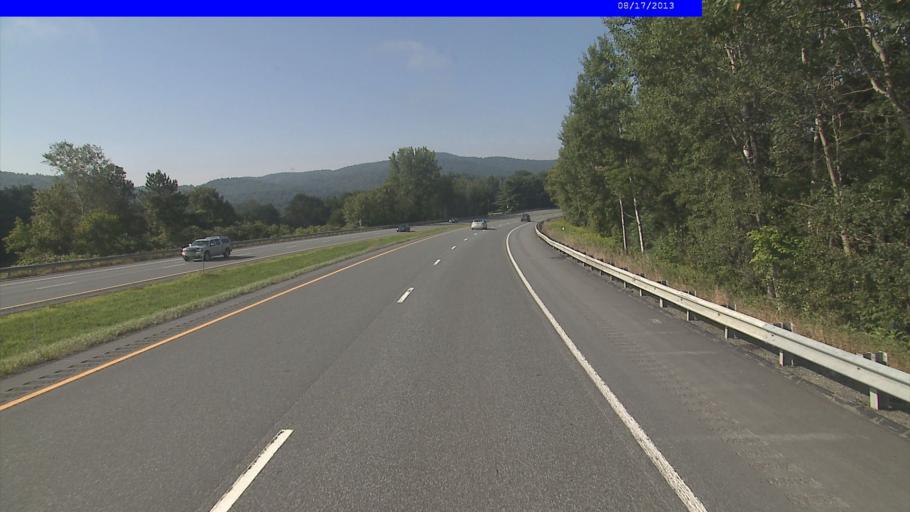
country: US
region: Vermont
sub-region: Windsor County
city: White River Junction
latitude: 43.5974
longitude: -72.3451
